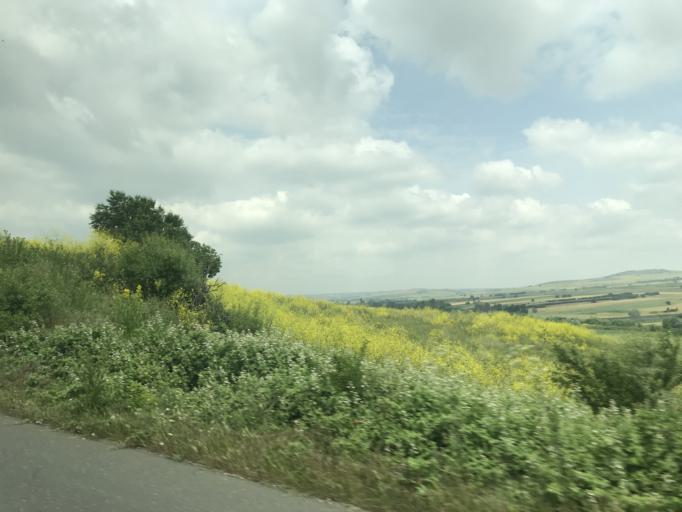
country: TR
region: Tekirdag
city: Tekirdag
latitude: 40.9914
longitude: 27.5662
